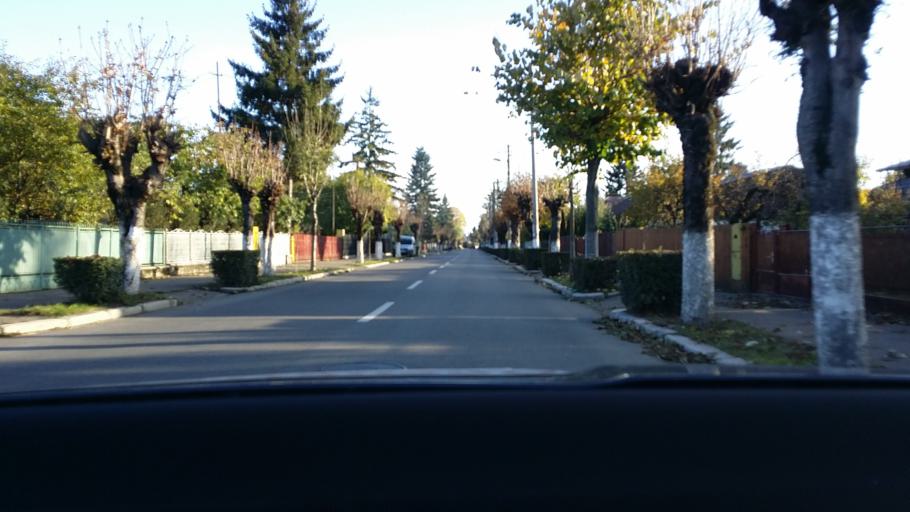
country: RO
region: Prahova
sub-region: Municipiul Campina
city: Campina
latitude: 45.1383
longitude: 25.7360
